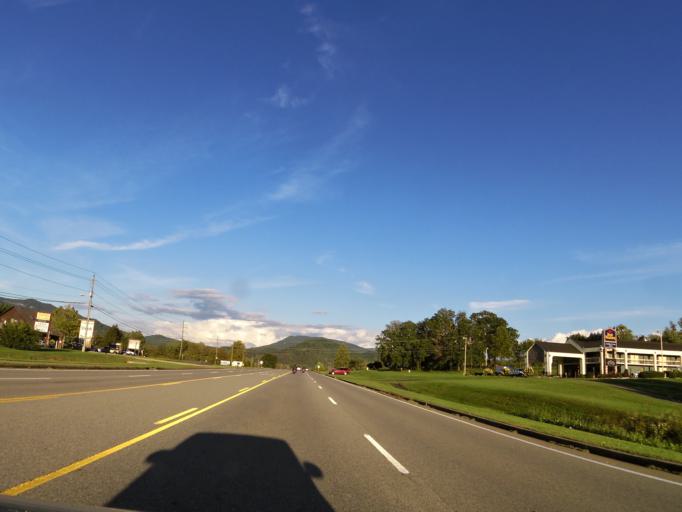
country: US
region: Tennessee
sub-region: Blount County
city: Wildwood
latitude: 35.6778
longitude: -83.7485
